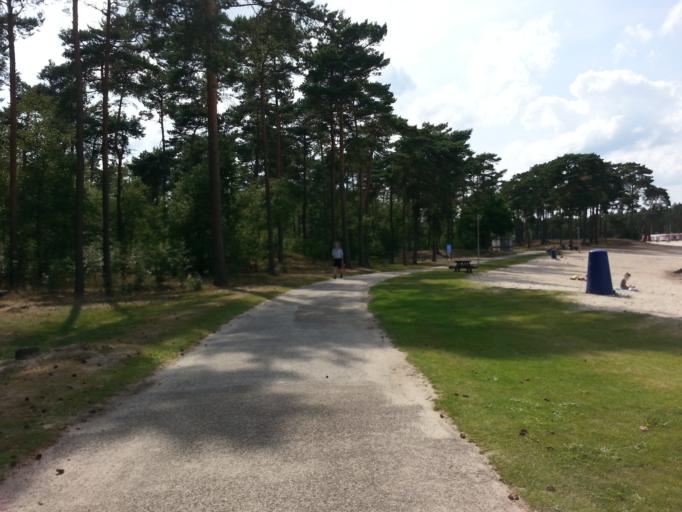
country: NL
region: Utrecht
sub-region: Gemeente Utrechtse Heuvelrug
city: Maarn
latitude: 52.0791
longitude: 5.3750
